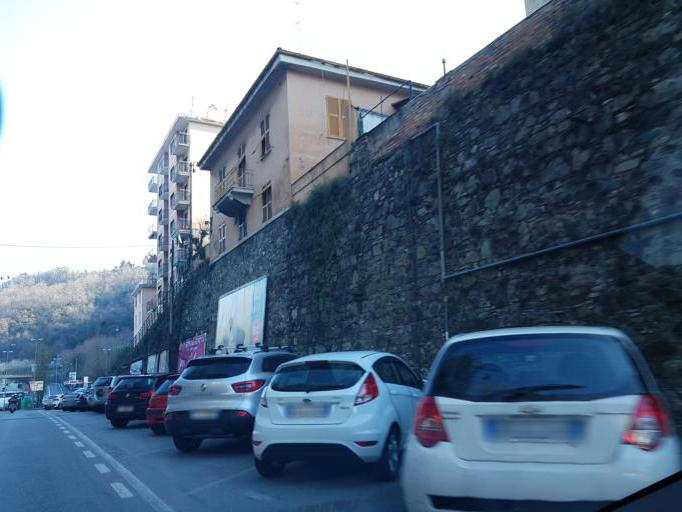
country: IT
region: Liguria
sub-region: Provincia di Genova
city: Manesseno
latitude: 44.4636
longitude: 8.9027
